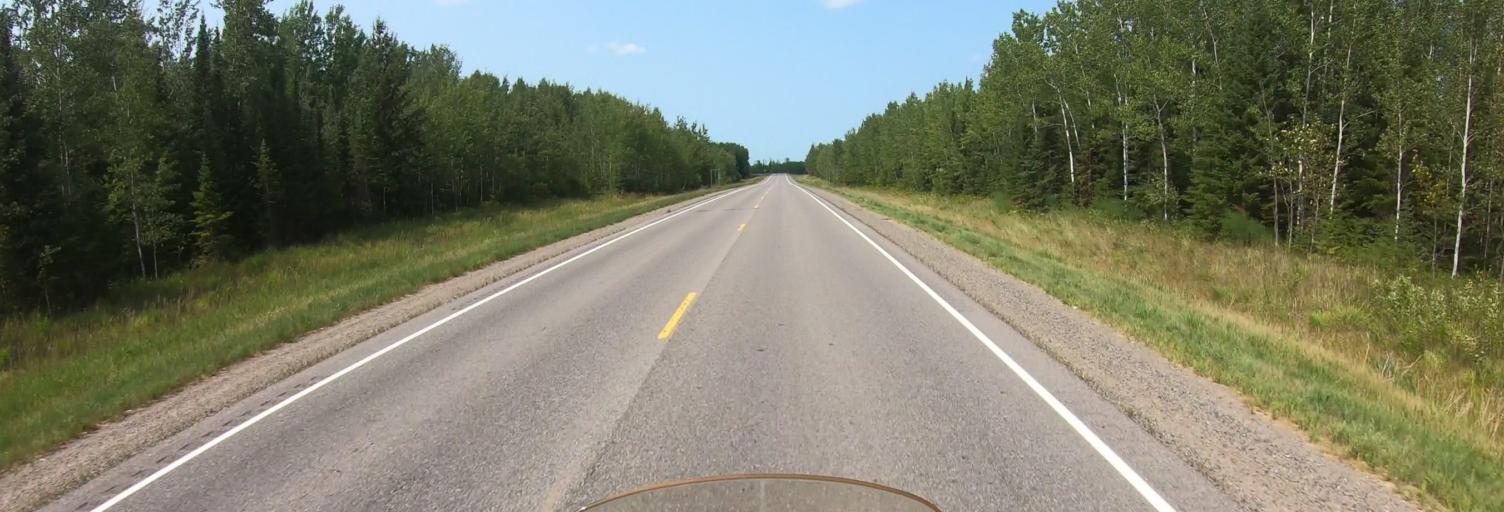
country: US
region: Minnesota
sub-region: Lake of the Woods County
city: Baudette
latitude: 48.6384
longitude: -94.1296
